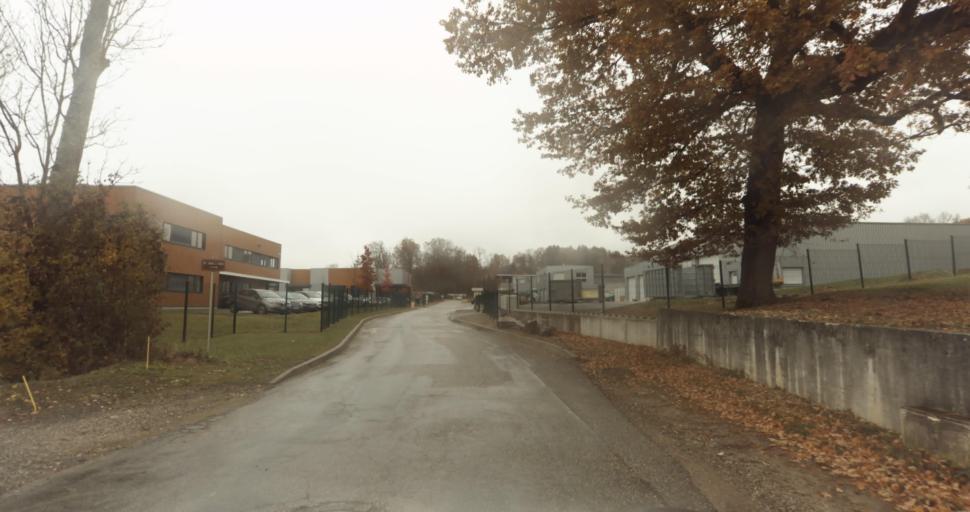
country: FR
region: Rhone-Alpes
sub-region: Departement de la Haute-Savoie
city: Saint-Martin-Bellevue
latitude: 45.9570
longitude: 6.1697
